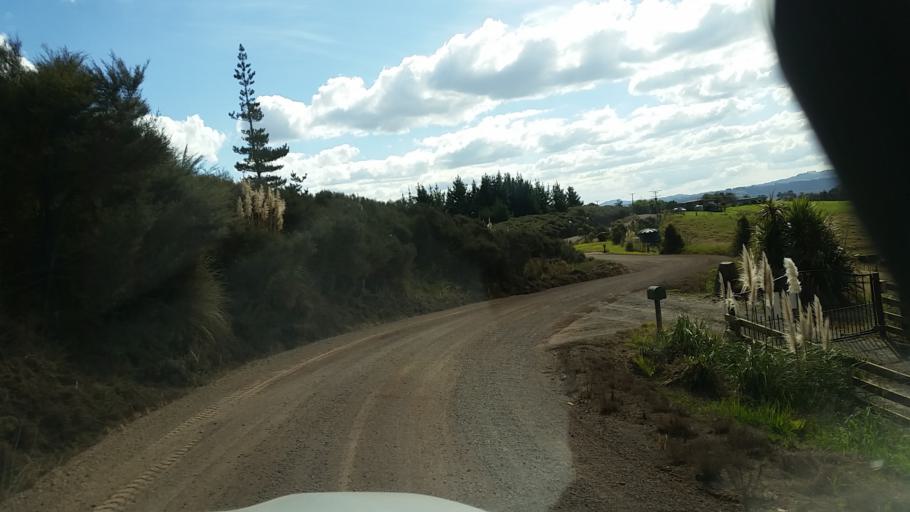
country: NZ
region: Northland
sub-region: Whangarei
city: Whangarei
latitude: -35.5890
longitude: 174.3162
